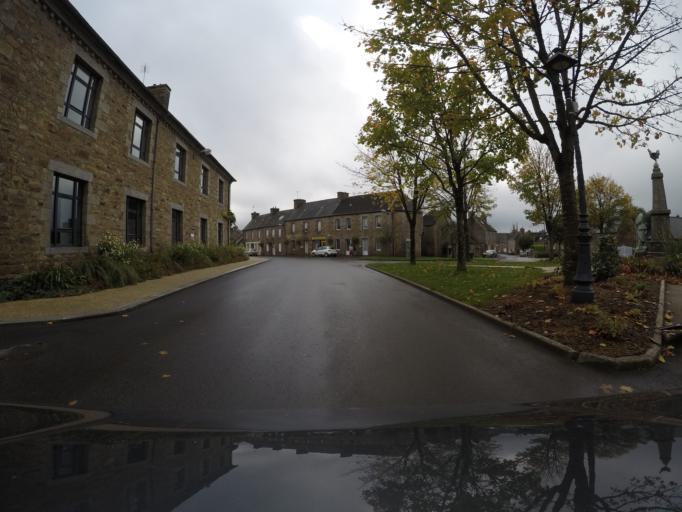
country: FR
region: Brittany
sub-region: Departement des Cotes-d'Armor
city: Louargat
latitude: 48.5668
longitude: -3.3408
